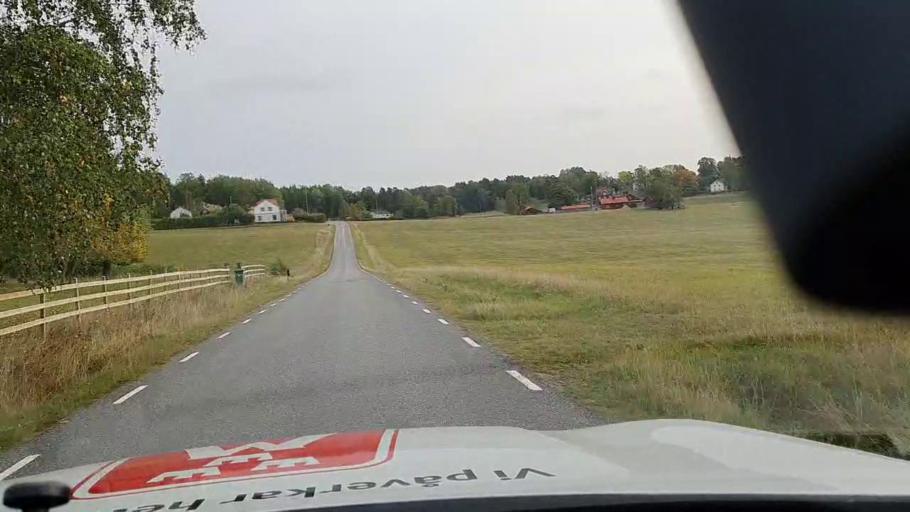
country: SE
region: Soedermanland
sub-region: Nykopings Kommun
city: Stigtomta
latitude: 58.9825
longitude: 16.9212
